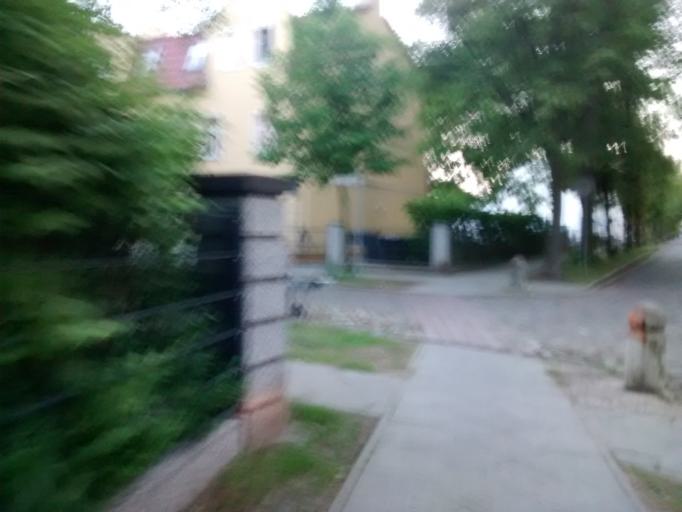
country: DE
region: Brandenburg
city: Hohen Neuendorf
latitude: 52.6691
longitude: 13.2838
